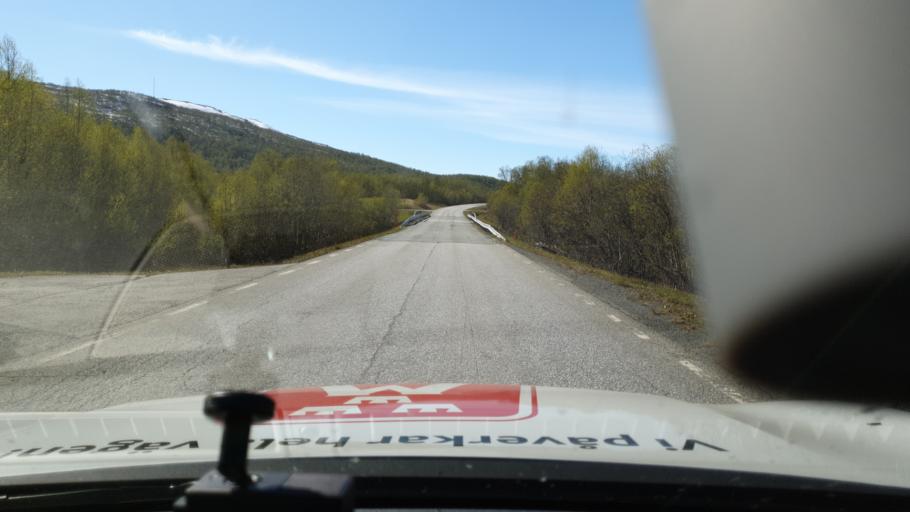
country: NO
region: Nordland
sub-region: Rana
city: Mo i Rana
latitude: 65.7804
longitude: 15.1268
